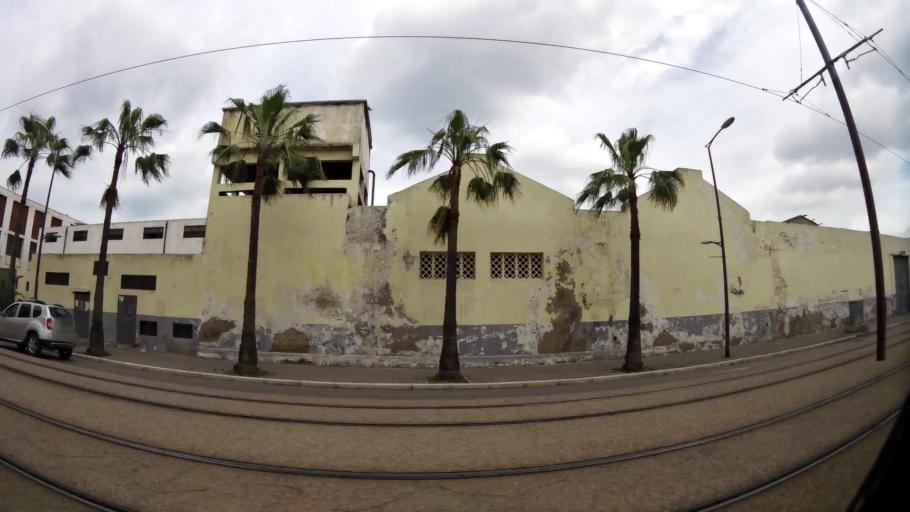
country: MA
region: Grand Casablanca
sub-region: Casablanca
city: Casablanca
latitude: 33.5912
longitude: -7.5759
